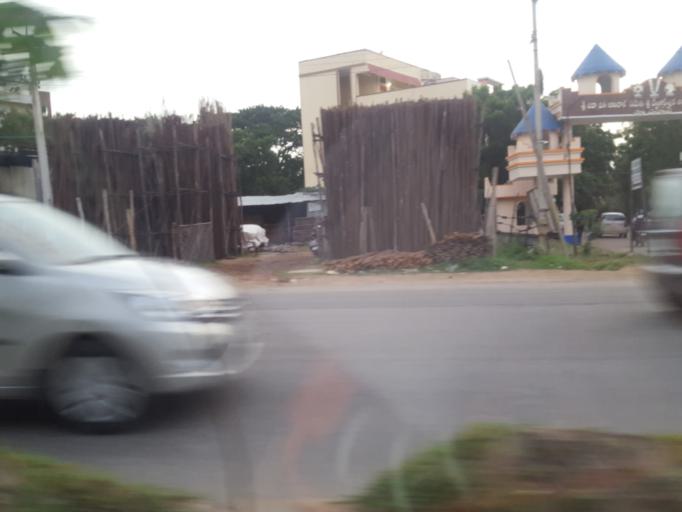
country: IN
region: Telangana
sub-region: Medak
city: Serilingampalle
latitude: 17.5181
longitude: 78.3565
